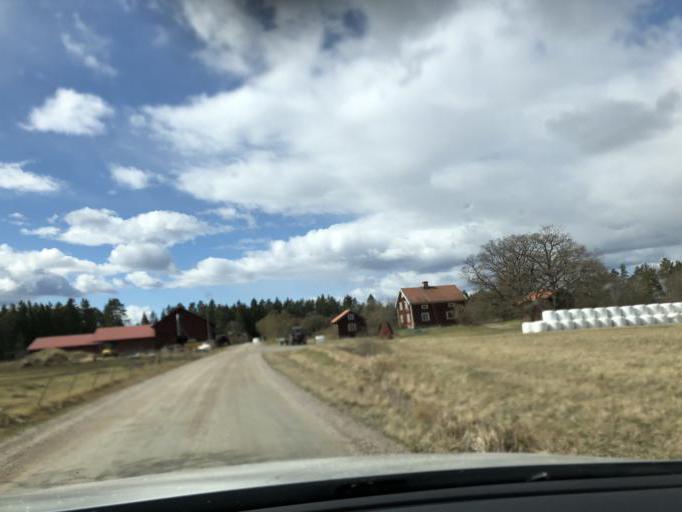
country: SE
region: Gaevleborg
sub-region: Gavle Kommun
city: Hedesunda
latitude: 60.3089
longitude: 17.1112
